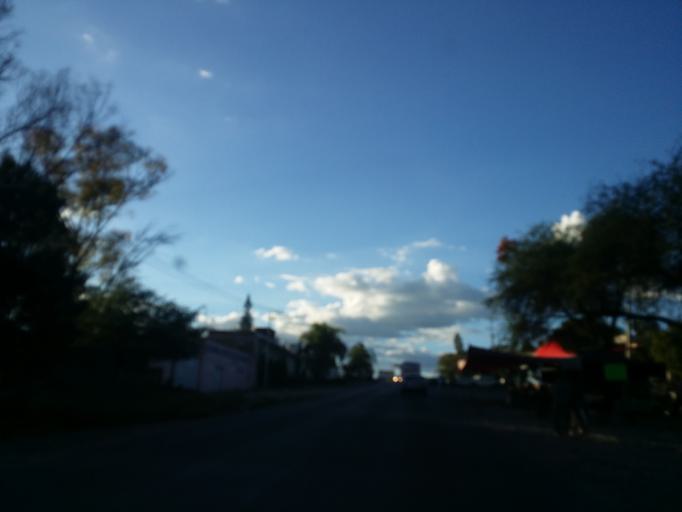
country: MX
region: Guanajuato
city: Leon
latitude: 21.1995
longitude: -101.6718
